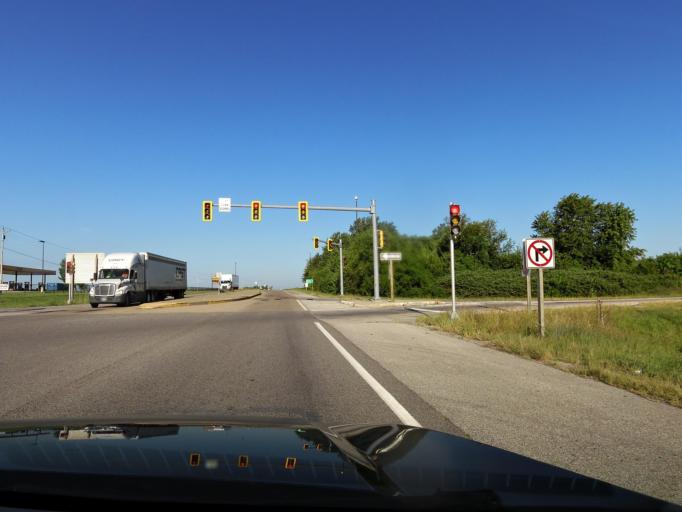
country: US
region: Illinois
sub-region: Clinton County
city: New Baden
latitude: 38.5355
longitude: -89.7311
